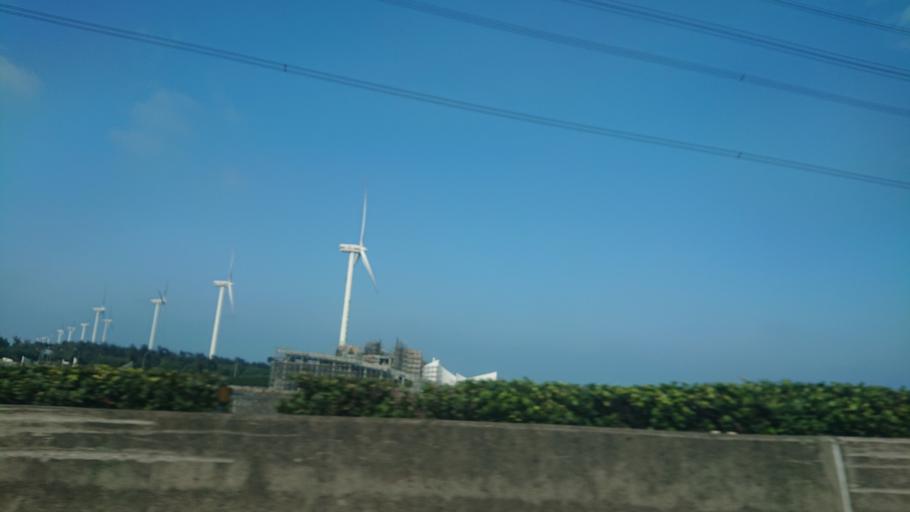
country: TW
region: Taiwan
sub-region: Changhua
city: Chang-hua
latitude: 24.1568
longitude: 120.4585
